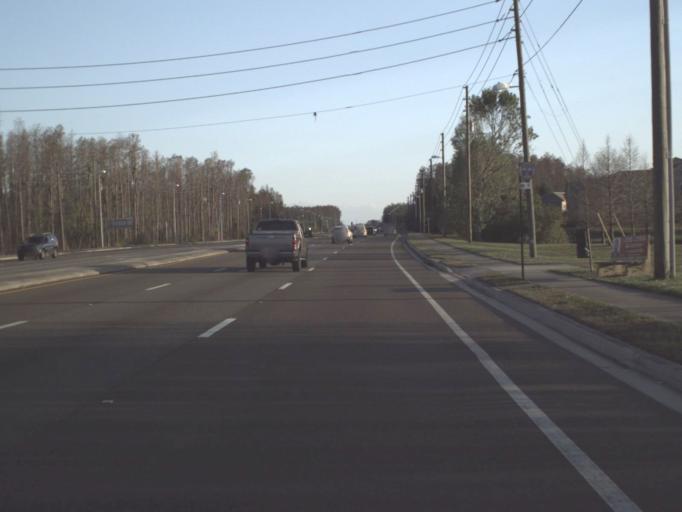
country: US
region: Florida
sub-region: Orange County
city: Hunters Creek
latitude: 28.3617
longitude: -81.4046
